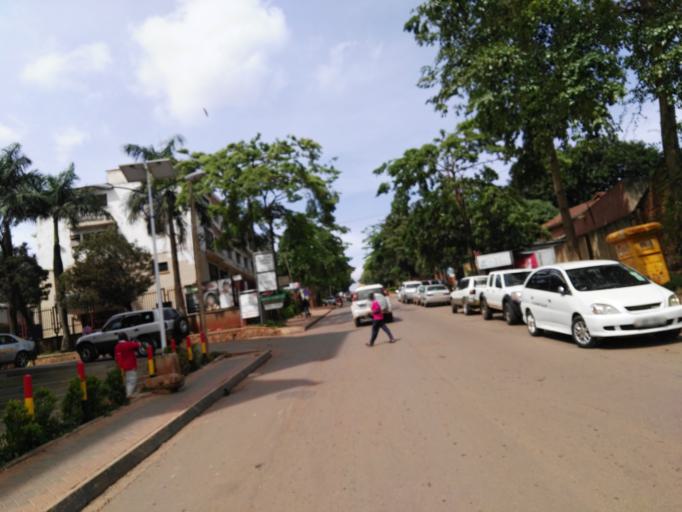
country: UG
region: Central Region
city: Kampala Central Division
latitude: 0.3188
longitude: 32.5756
